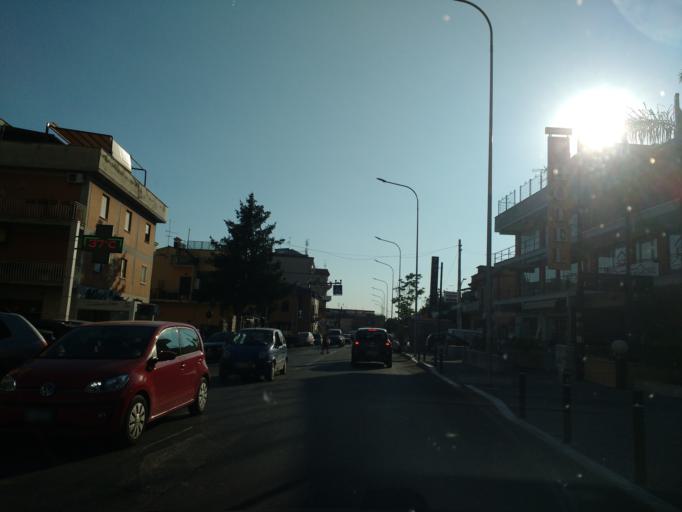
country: IT
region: Latium
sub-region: Citta metropolitana di Roma Capitale
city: Villa Adriana
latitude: 41.9567
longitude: 12.7736
